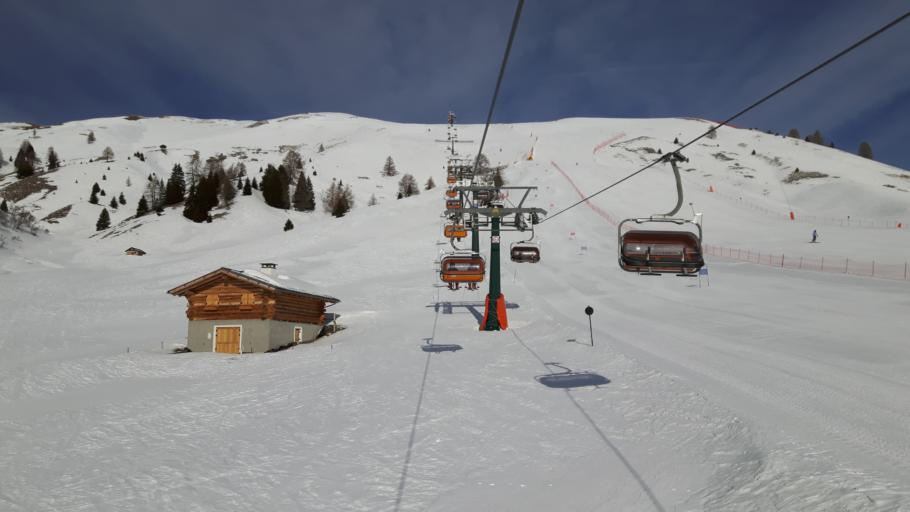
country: IT
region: Trentino-Alto Adige
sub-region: Provincia di Trento
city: Moena
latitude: 46.3364
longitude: 11.6983
